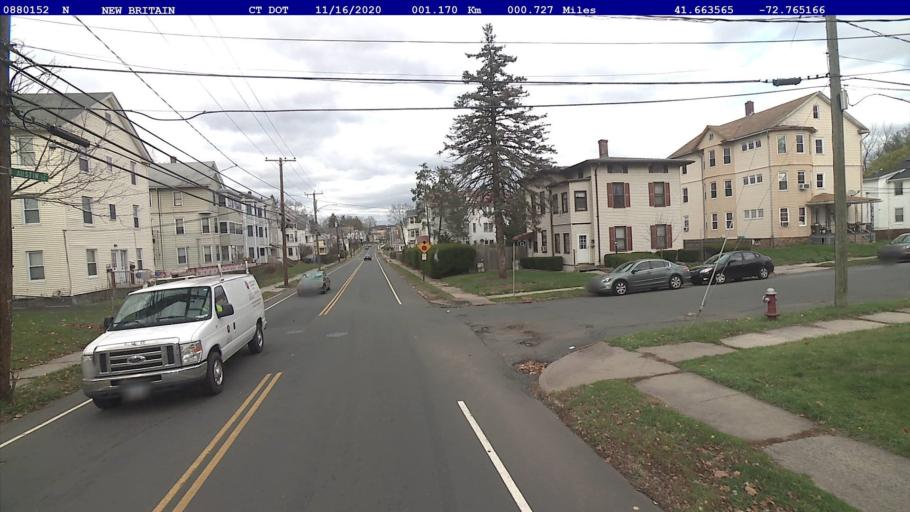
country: US
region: Connecticut
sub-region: Hartford County
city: New Britain
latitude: 41.6636
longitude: -72.7652
